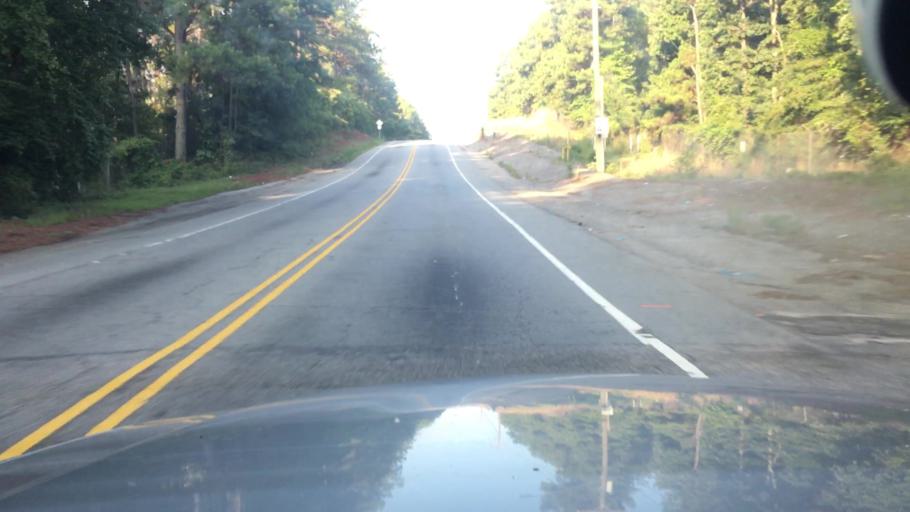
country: US
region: North Carolina
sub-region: Cumberland County
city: Spring Lake
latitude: 35.1074
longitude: -78.9433
